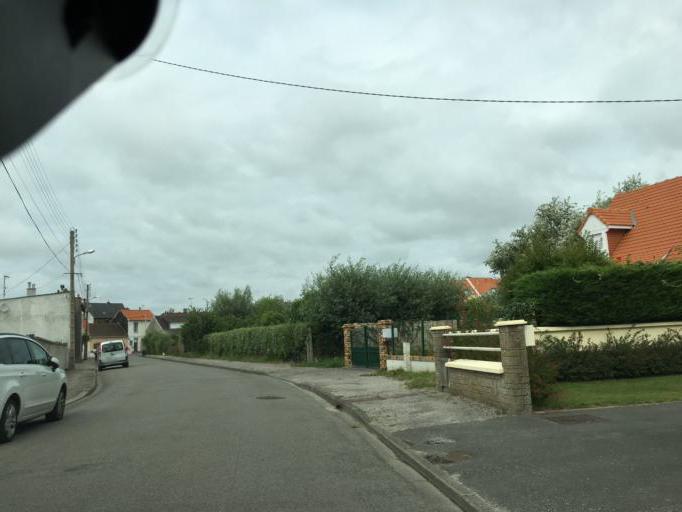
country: FR
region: Nord-Pas-de-Calais
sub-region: Departement du Pas-de-Calais
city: Berck
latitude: 50.4066
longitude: 1.5878
